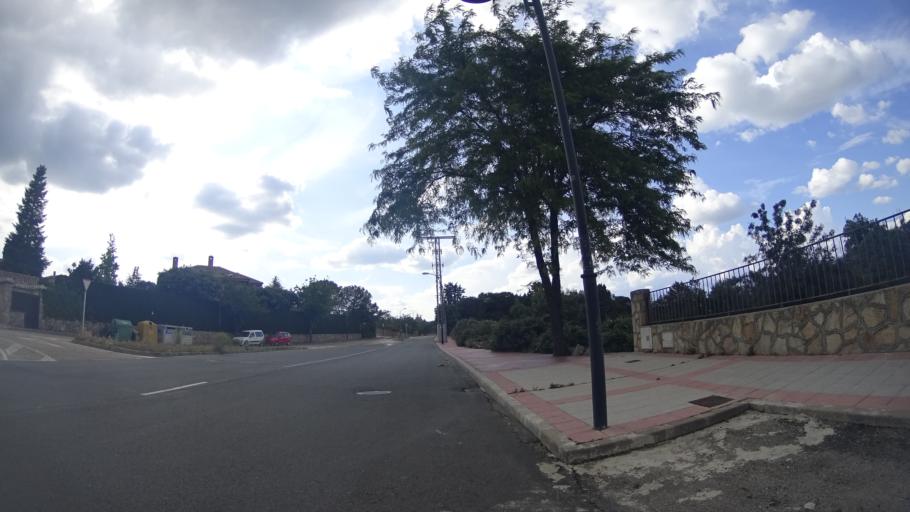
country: ES
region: Madrid
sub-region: Provincia de Madrid
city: Galapagar
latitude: 40.5716
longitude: -3.9912
